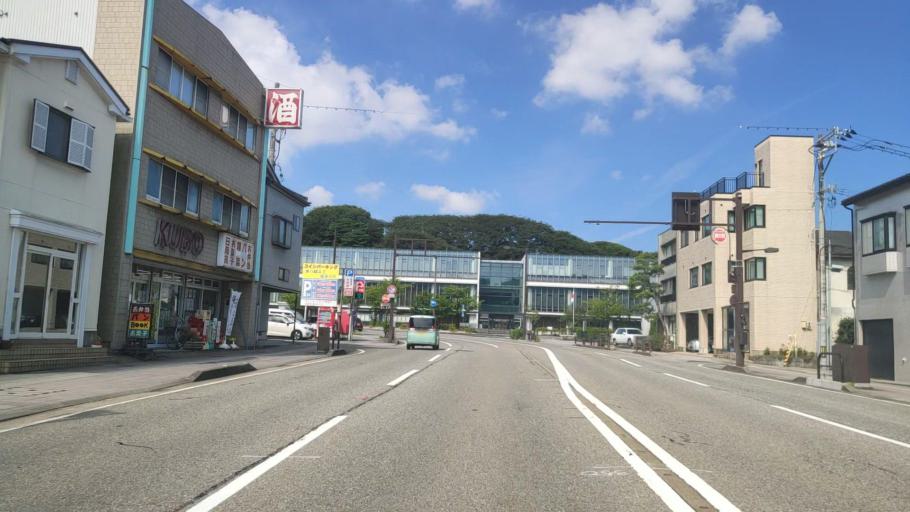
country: JP
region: Ishikawa
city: Kanazawa-shi
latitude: 36.5670
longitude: 136.6639
